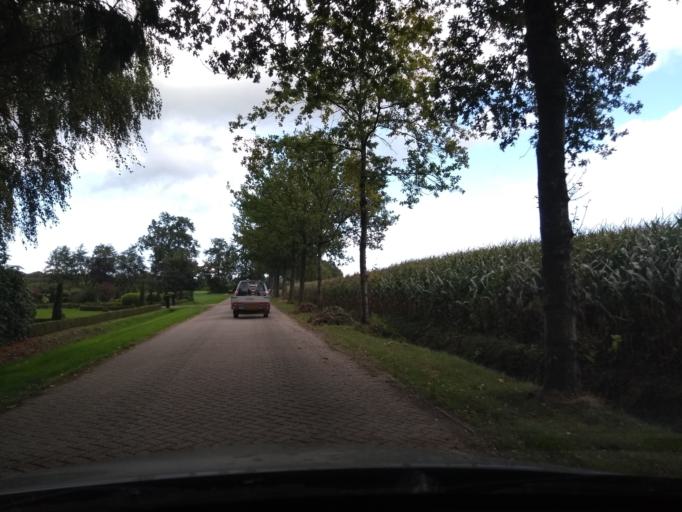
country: NL
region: Overijssel
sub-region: Gemeente Raalte
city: Raalte
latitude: 52.3724
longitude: 6.3183
